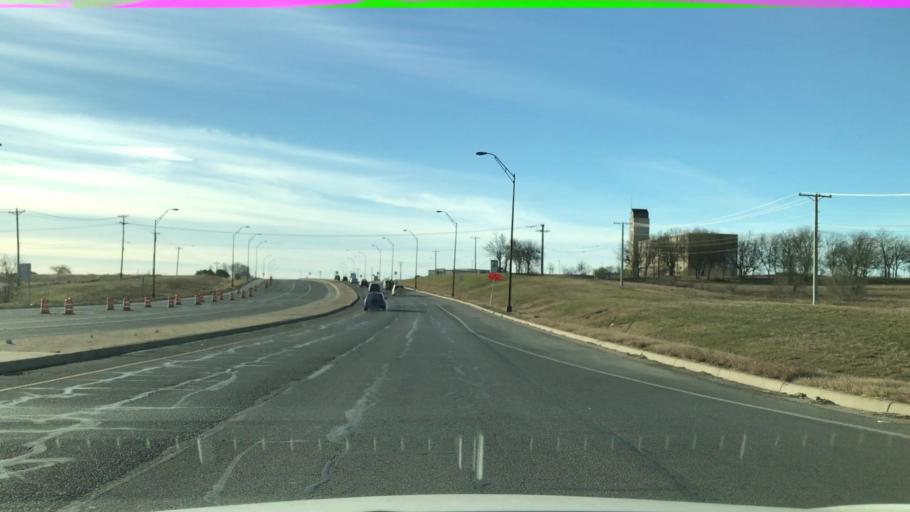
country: US
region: Texas
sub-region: Williamson County
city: Georgetown
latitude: 30.5722
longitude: -97.6505
